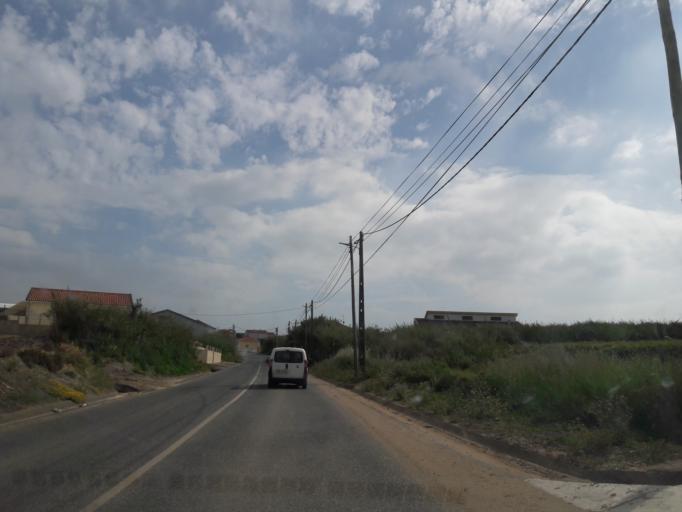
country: PT
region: Leiria
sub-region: Peniche
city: Atouguia da Baleia
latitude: 39.3448
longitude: -9.3274
